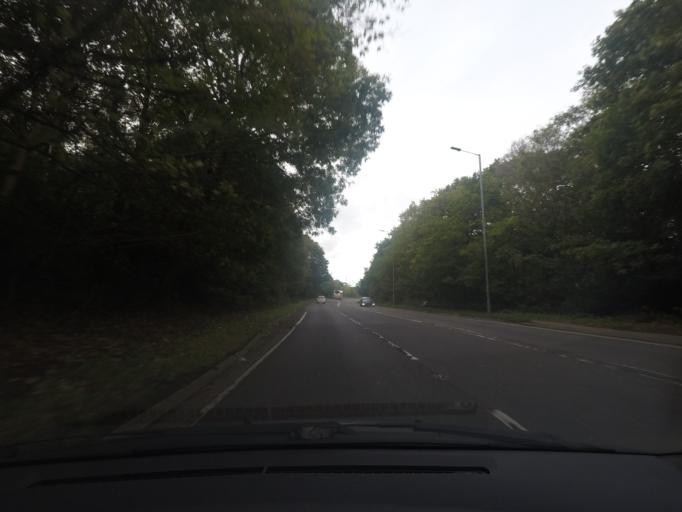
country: GB
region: England
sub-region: Sheffield
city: Chapletown
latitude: 53.4830
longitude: -1.4952
